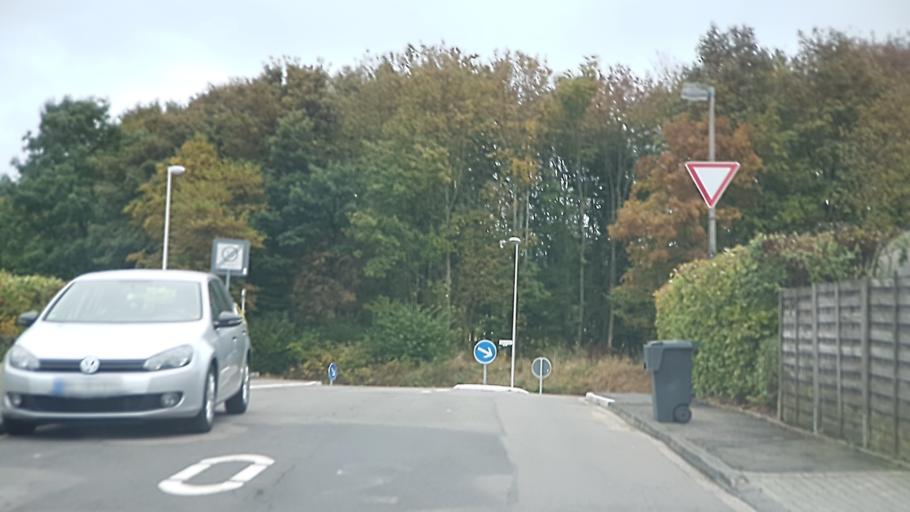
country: DE
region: North Rhine-Westphalia
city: Meinerzhagen
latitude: 51.1135
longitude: 7.6462
